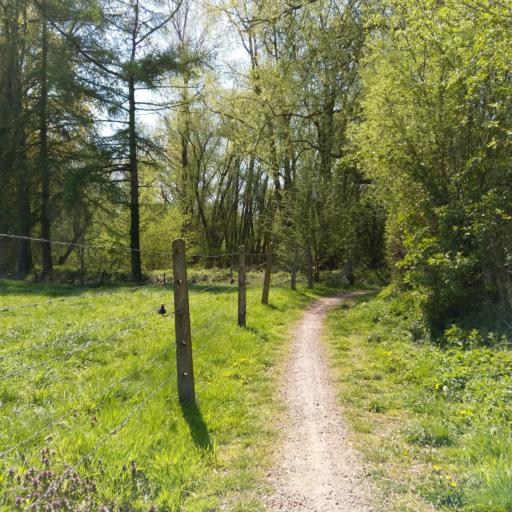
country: BE
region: Wallonia
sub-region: Province du Hainaut
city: Lens
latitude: 50.5475
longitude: 3.8955
